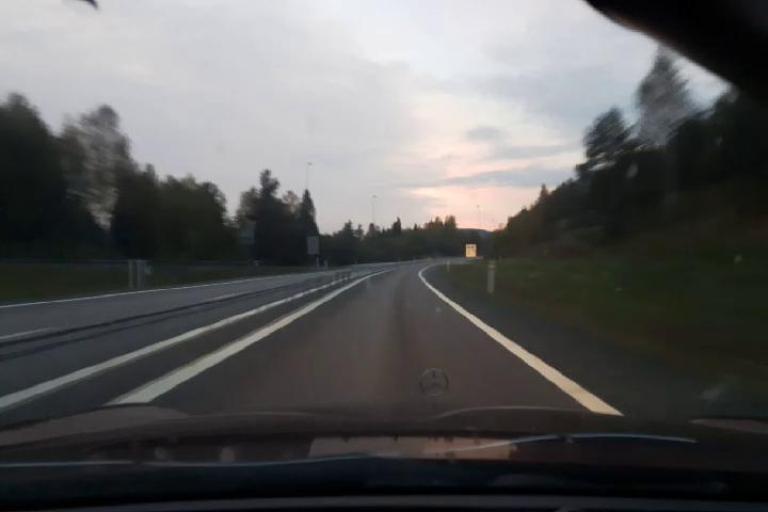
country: SE
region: Vaesternorrland
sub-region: Kramfors Kommun
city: Nordingra
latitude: 62.9397
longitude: 18.0938
